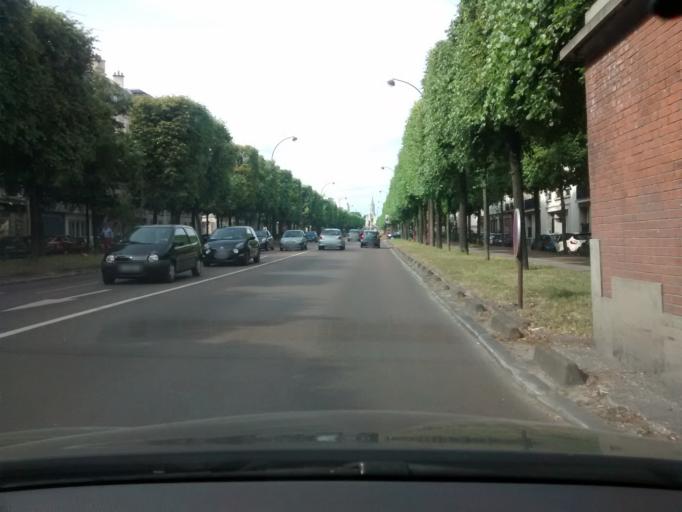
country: FR
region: Ile-de-France
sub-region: Departement des Yvelines
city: Versailles
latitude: 48.8099
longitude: 2.1258
